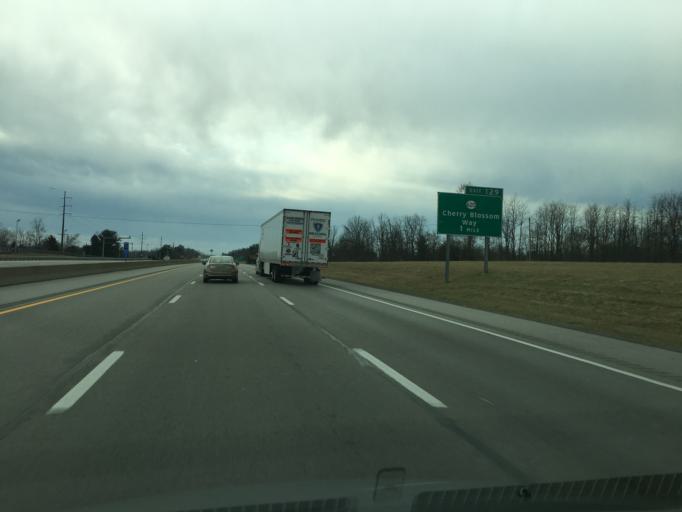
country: US
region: Kentucky
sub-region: Scott County
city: Georgetown
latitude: 38.2941
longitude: -84.5589
